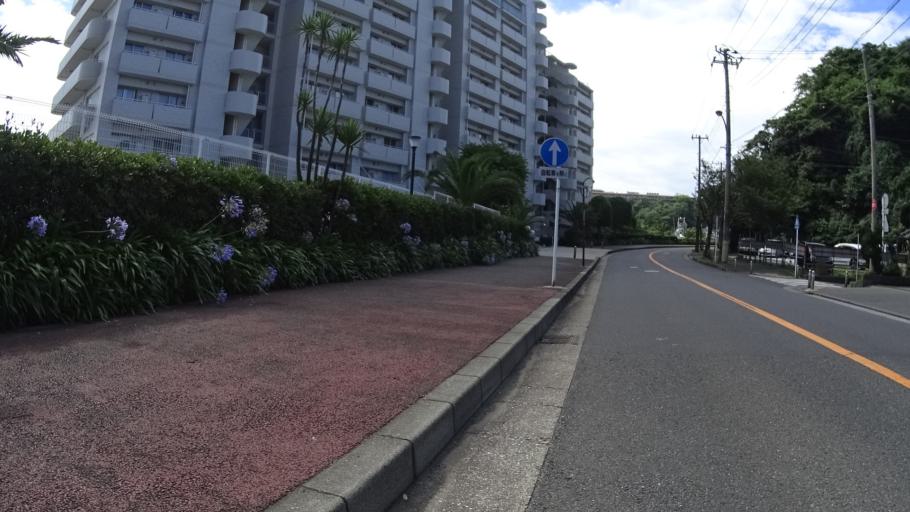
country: JP
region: Kanagawa
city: Yokosuka
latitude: 35.2363
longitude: 139.7225
